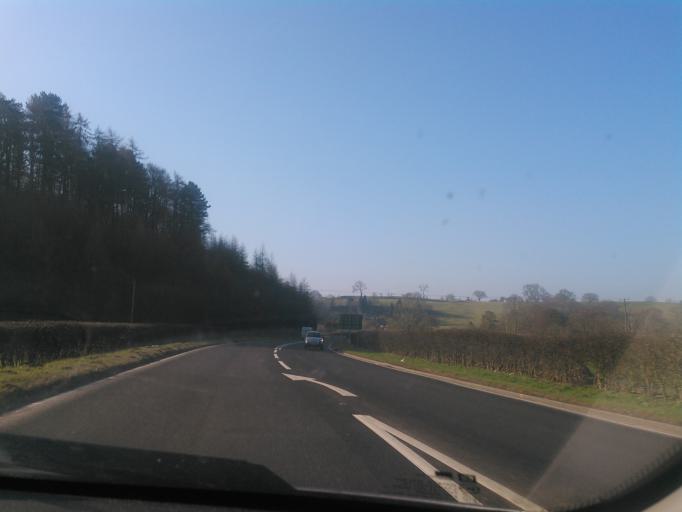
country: GB
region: England
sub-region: Shropshire
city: Church Stretton
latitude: 52.5148
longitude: -2.8229
